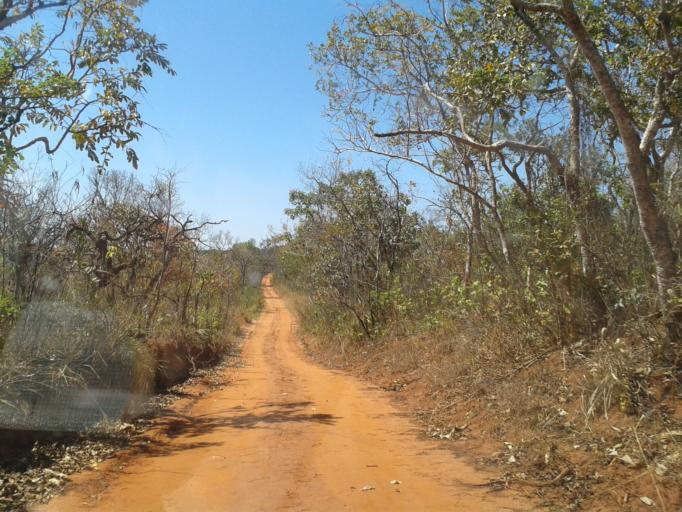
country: BR
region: Minas Gerais
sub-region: Monte Alegre De Minas
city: Monte Alegre de Minas
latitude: -18.8328
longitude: -49.1000
